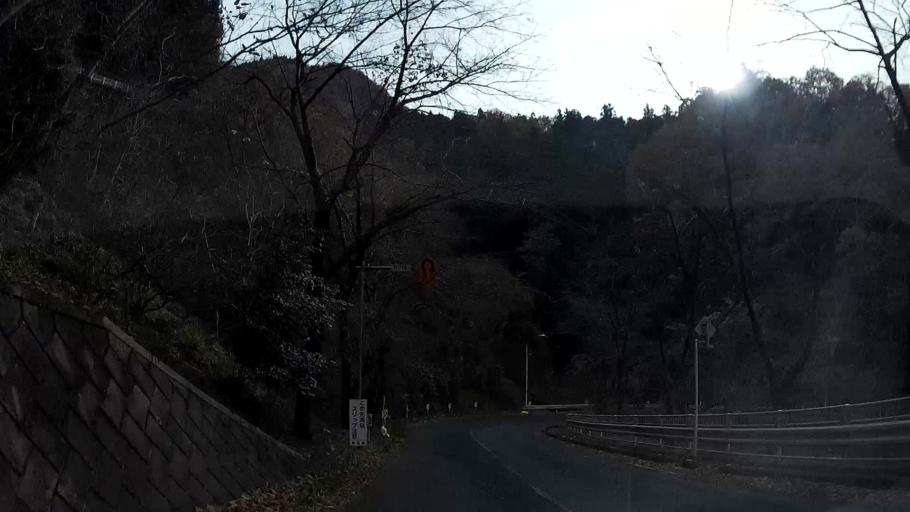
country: JP
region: Saitama
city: Chichibu
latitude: 35.9573
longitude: 139.0554
